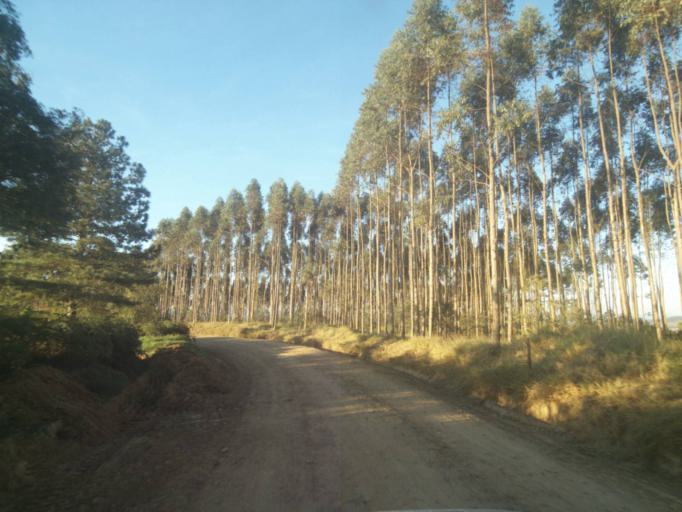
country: BR
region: Parana
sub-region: Tibagi
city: Tibagi
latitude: -24.5466
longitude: -50.5323
